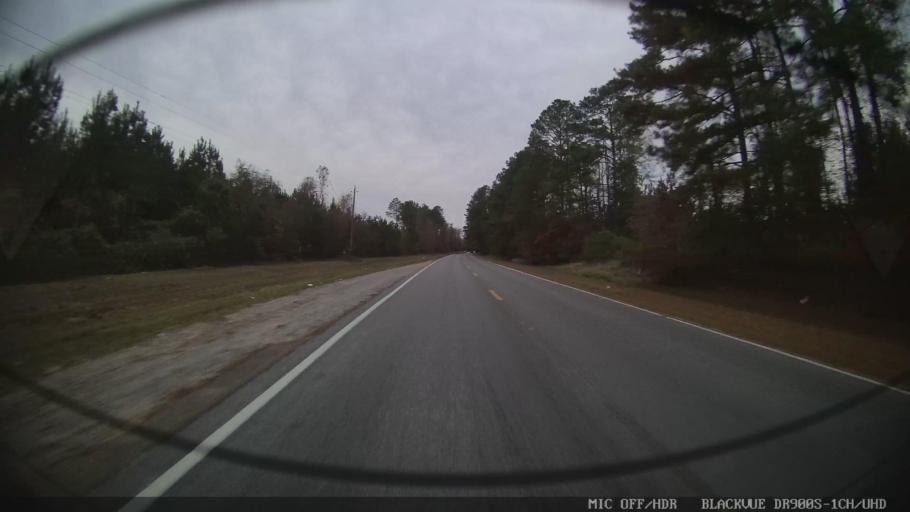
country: US
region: Mississippi
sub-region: Clarke County
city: Quitman
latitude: 32.0244
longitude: -88.8437
